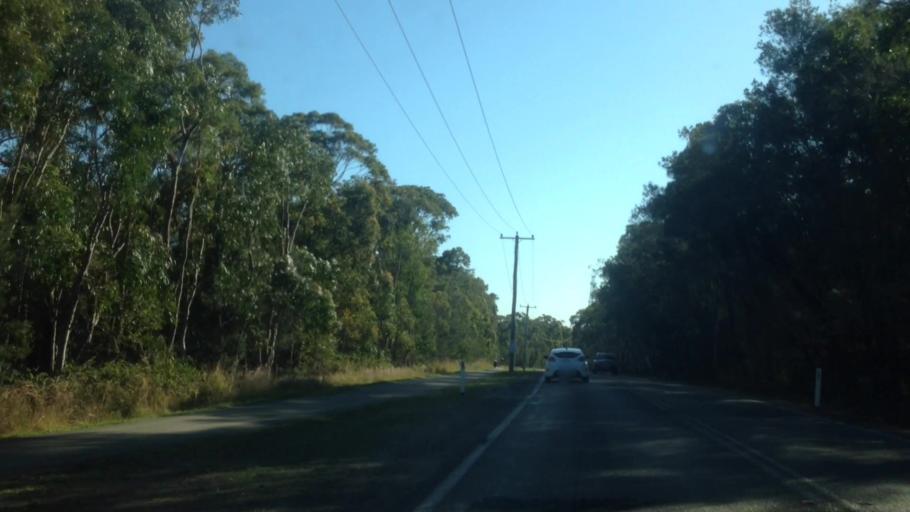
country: AU
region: New South Wales
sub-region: Lake Macquarie Shire
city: Dora Creek
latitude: -33.1119
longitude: 151.5236
